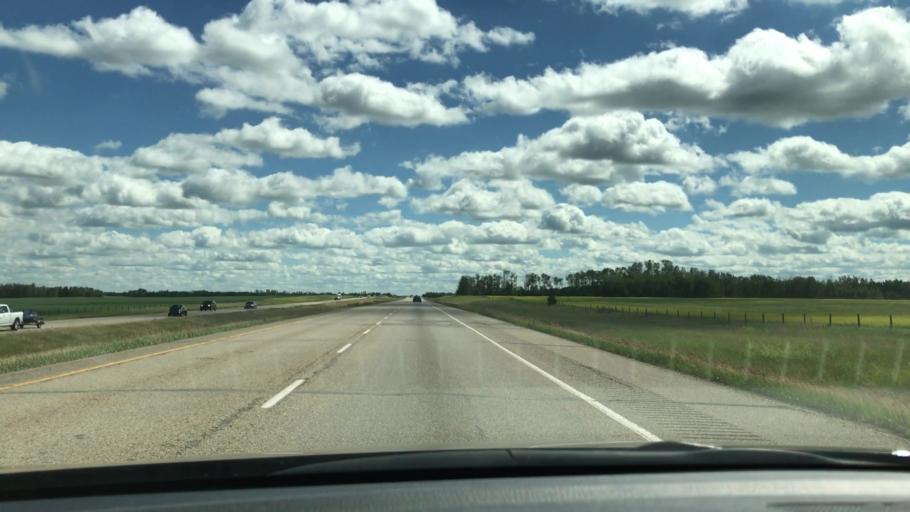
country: CA
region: Alberta
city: Millet
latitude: 53.1315
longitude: -113.5984
